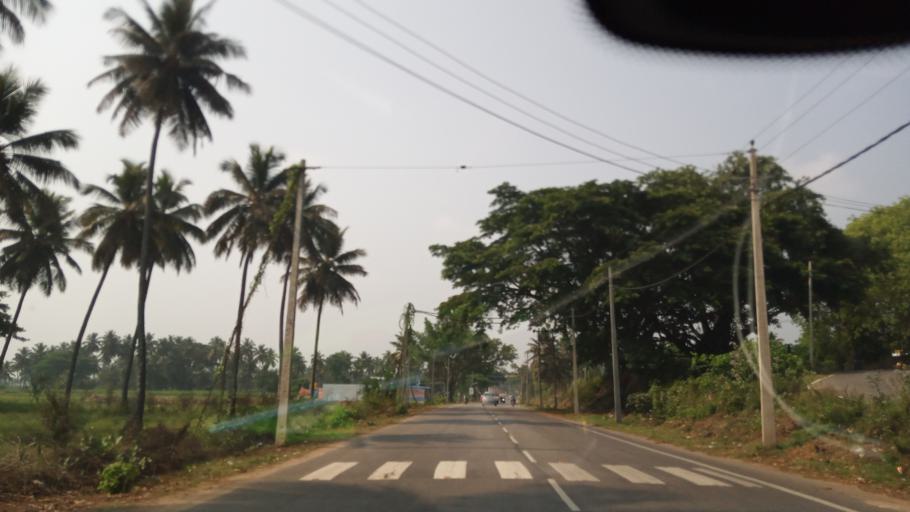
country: IN
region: Karnataka
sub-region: Mandya
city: Pandavapura
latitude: 12.5131
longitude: 76.6747
